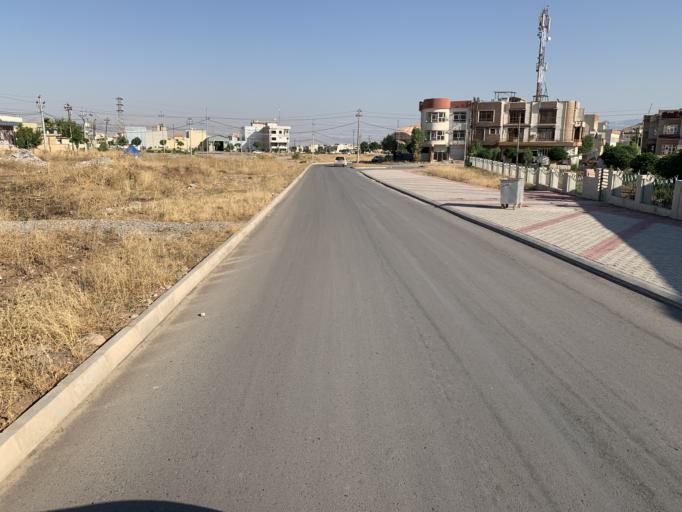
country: IQ
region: As Sulaymaniyah
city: Raniye
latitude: 36.2399
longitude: 44.8709
